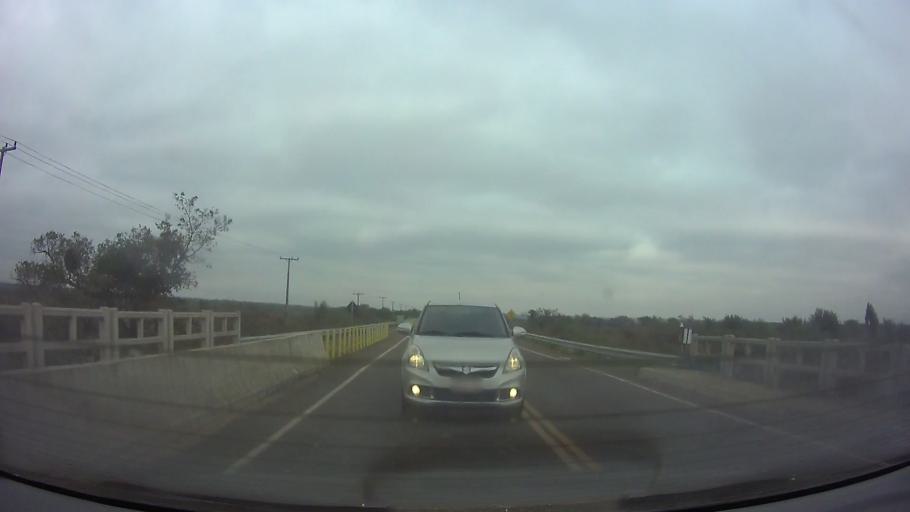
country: PY
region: Cordillera
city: Emboscada
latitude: -25.2043
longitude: -57.3705
